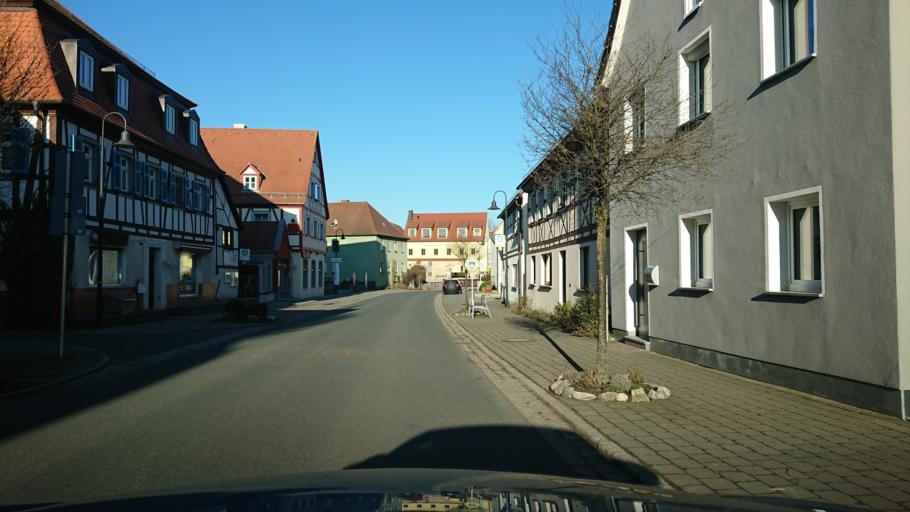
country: DE
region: Bavaria
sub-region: Upper Franconia
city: Kirchehrenbach
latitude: 49.7339
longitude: 11.1460
